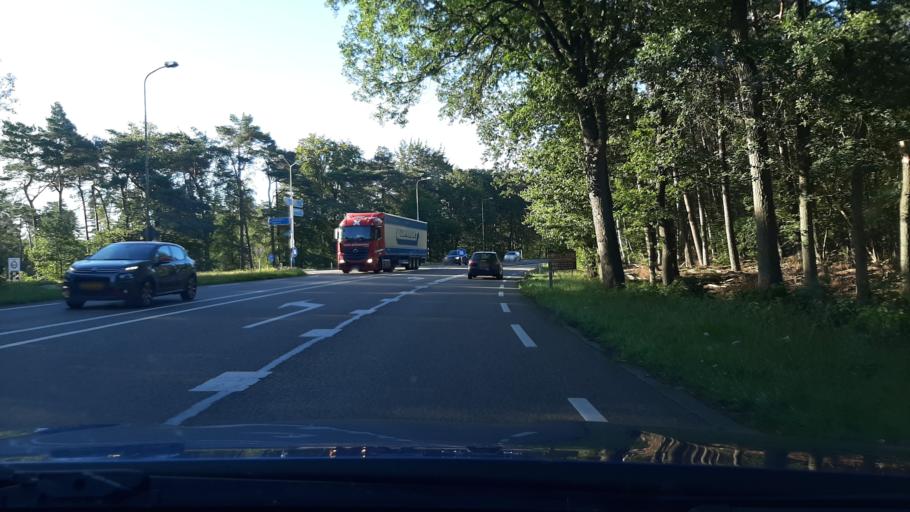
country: NL
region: Gelderland
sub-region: Gemeente Ermelo
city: Ermelo
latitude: 52.3080
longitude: 5.6816
